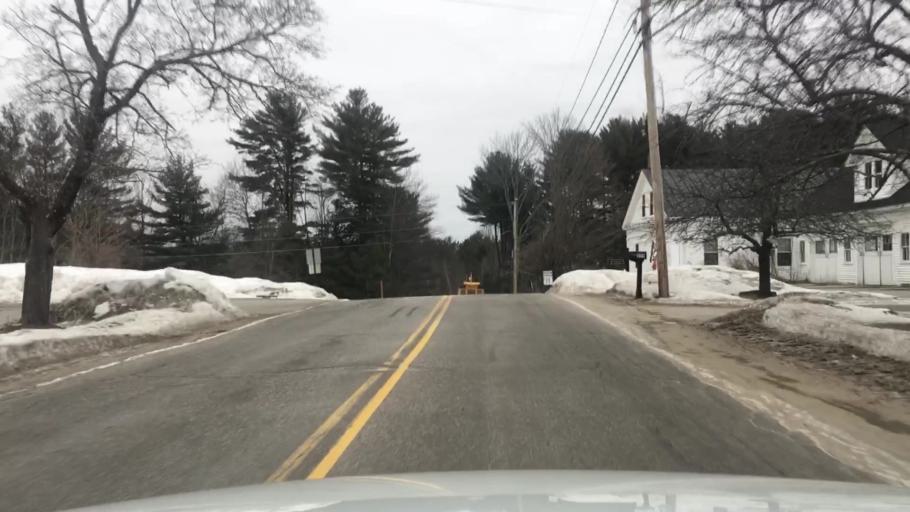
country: US
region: Maine
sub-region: York County
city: Shapleigh
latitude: 43.5405
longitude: -70.8479
